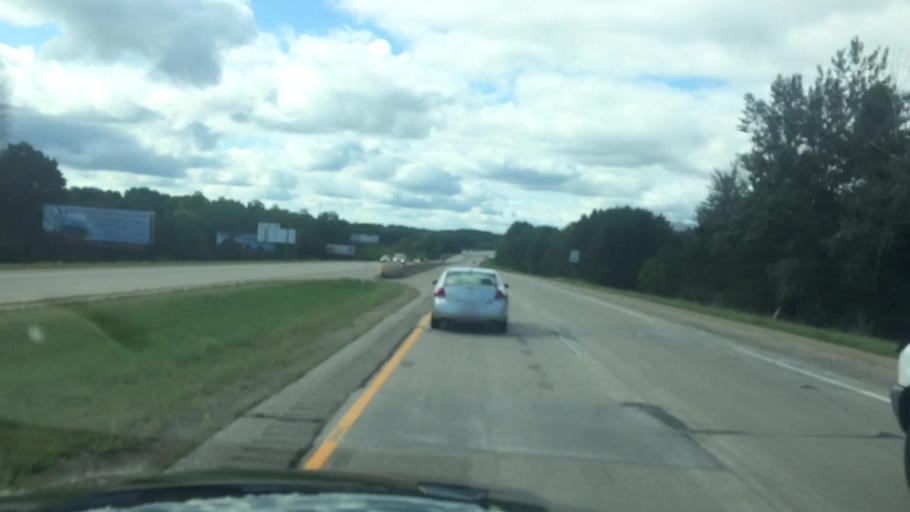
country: US
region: Wisconsin
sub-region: Waupaca County
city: Waupaca
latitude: 44.3407
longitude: -89.0803
